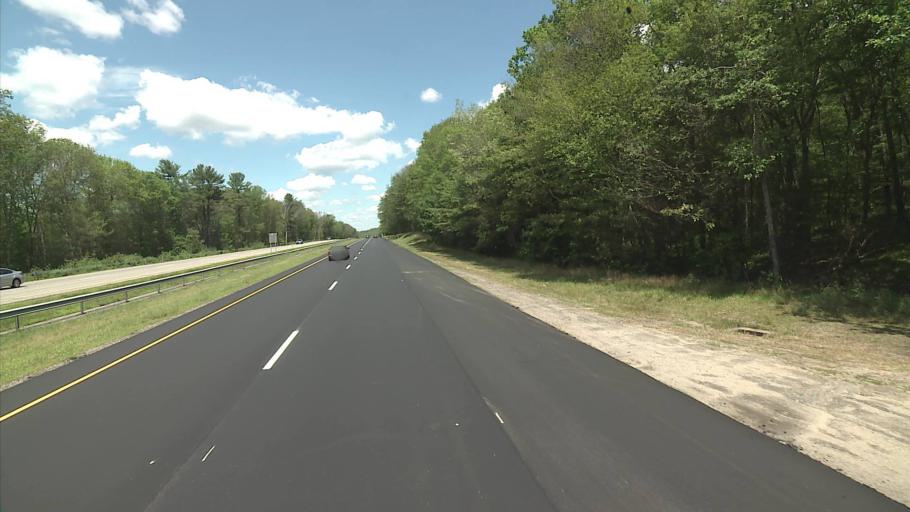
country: US
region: Connecticut
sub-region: Windham County
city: Danielson
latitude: 41.7719
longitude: -71.8721
